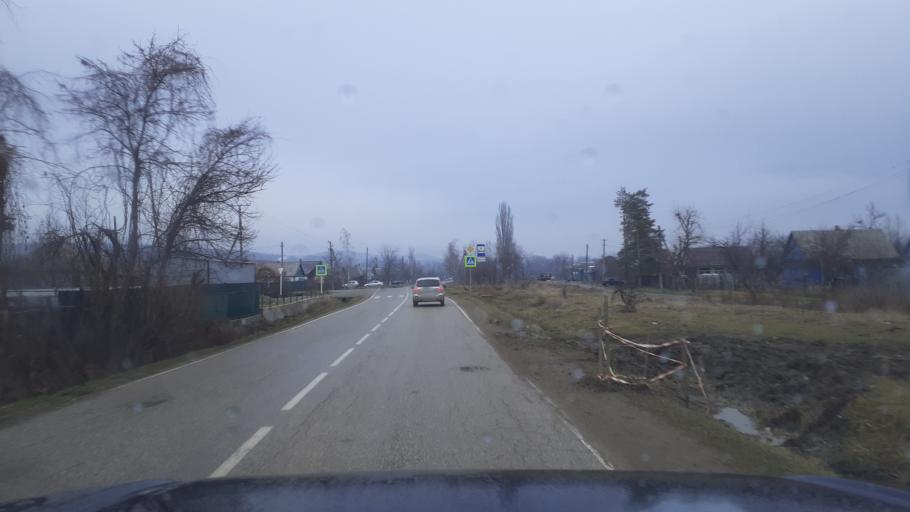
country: RU
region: Krasnodarskiy
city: Neftegorsk
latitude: 44.2492
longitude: 39.7664
